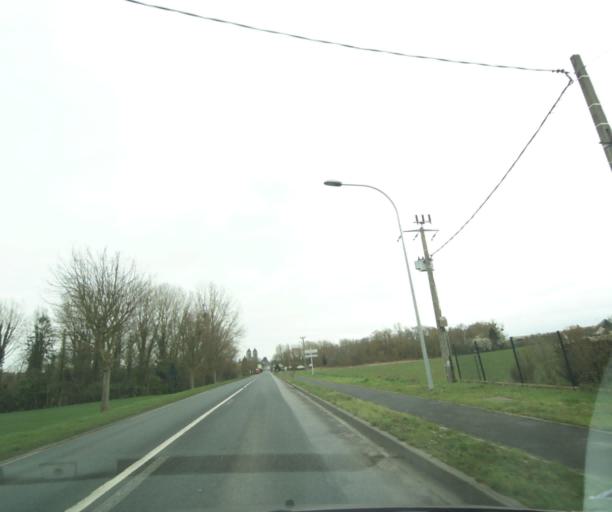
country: FR
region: Picardie
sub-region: Departement de l'Oise
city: Noyon
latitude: 49.5894
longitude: 2.9871
